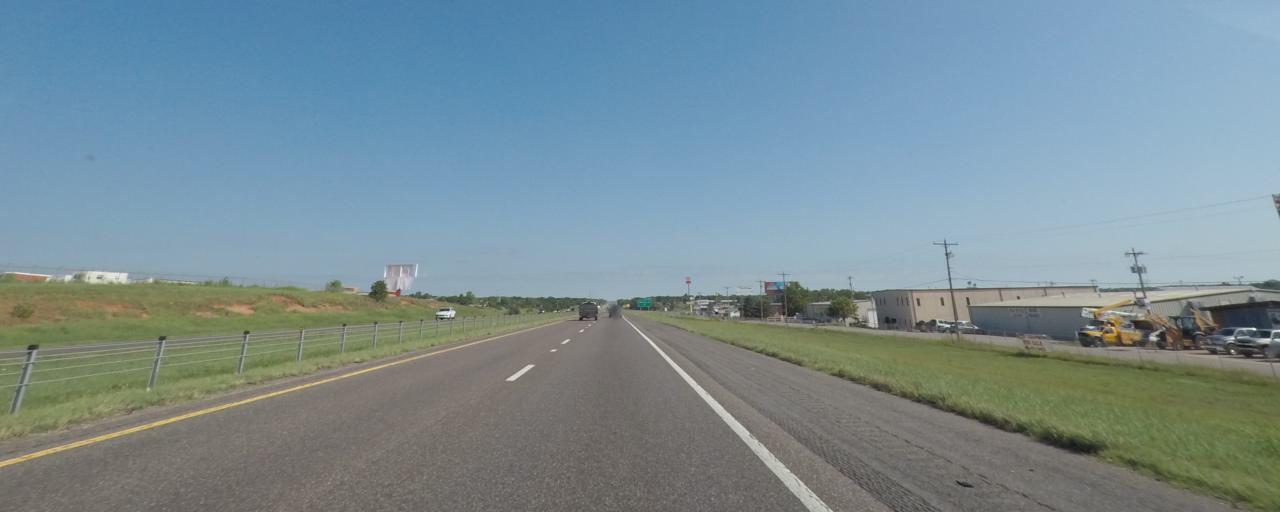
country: US
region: Oklahoma
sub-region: Oklahoma County
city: Edmond
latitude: 35.7176
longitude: -97.4162
